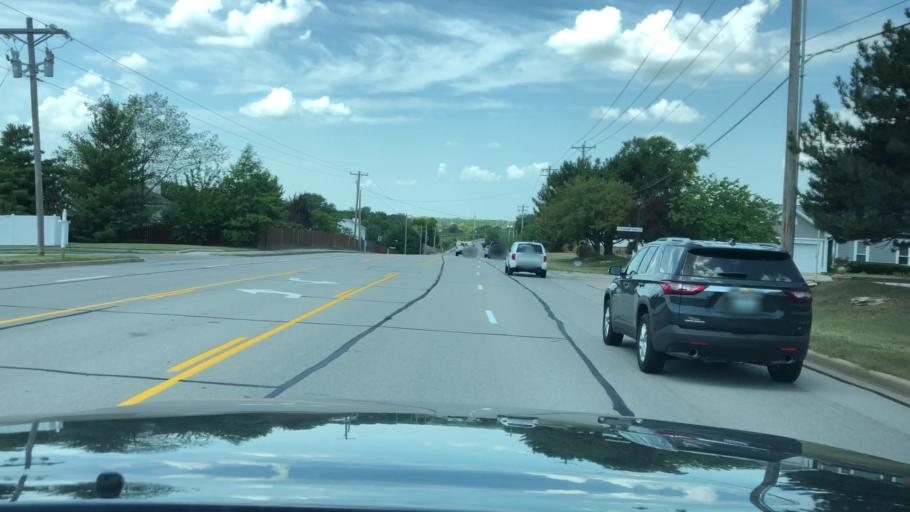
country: US
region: Missouri
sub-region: Saint Charles County
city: O'Fallon
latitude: 38.7889
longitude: -90.6767
